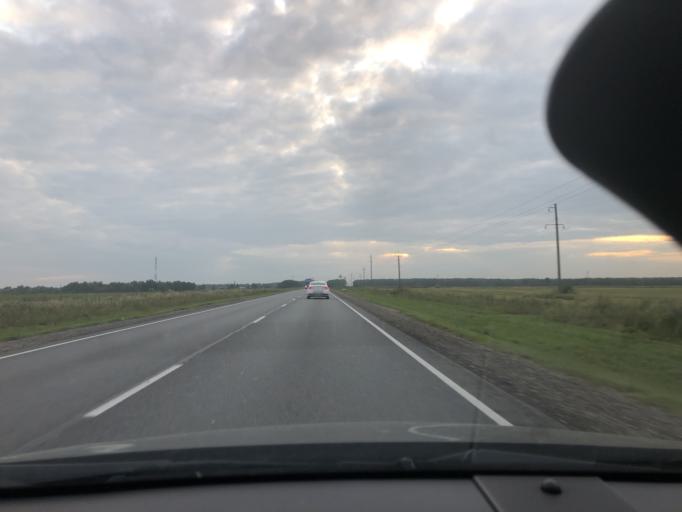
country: RU
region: Kaluga
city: Ferzikovo
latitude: 54.3679
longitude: 36.6978
